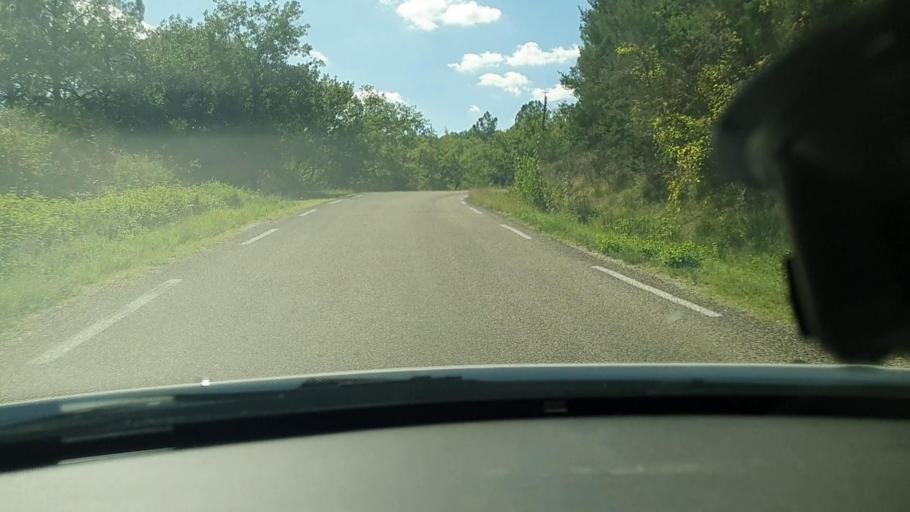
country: FR
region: Languedoc-Roussillon
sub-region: Departement du Gard
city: Goudargues
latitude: 44.1688
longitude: 4.4863
